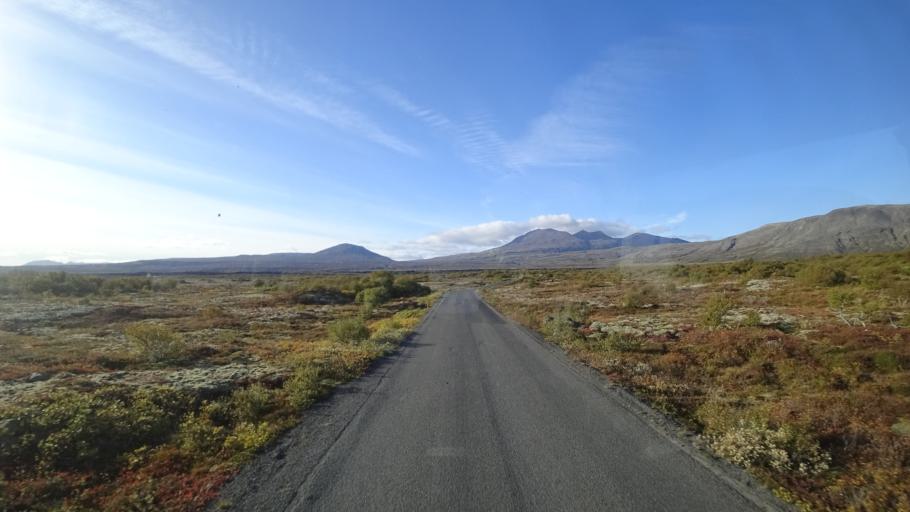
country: IS
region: South
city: Hveragerdi
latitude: 64.2728
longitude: -21.0712
